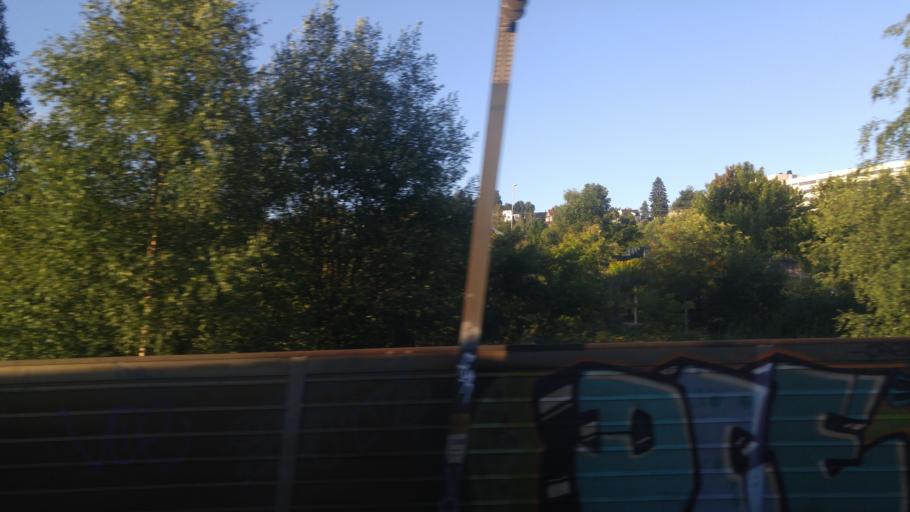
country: NO
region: Akershus
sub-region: Skedsmo
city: Lillestrom
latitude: 59.9527
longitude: 11.0249
